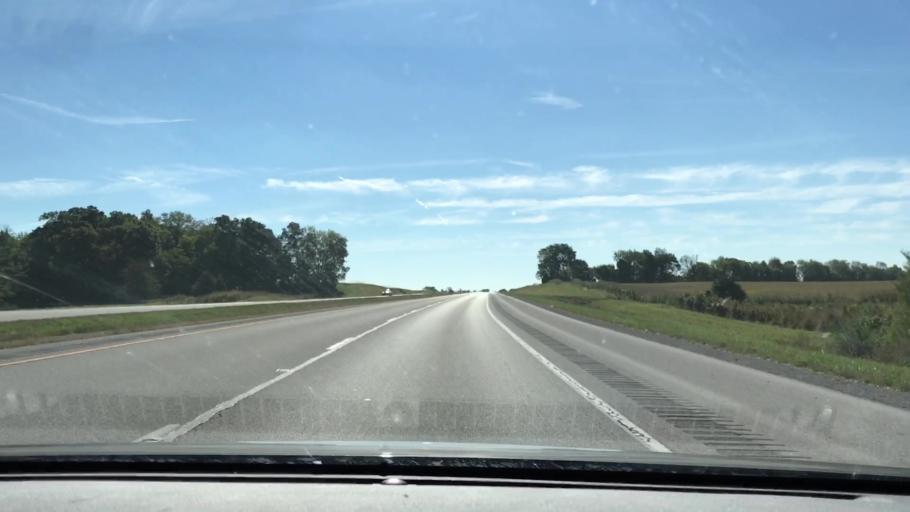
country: US
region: Kentucky
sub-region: Todd County
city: Elkton
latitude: 36.8210
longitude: -87.1452
